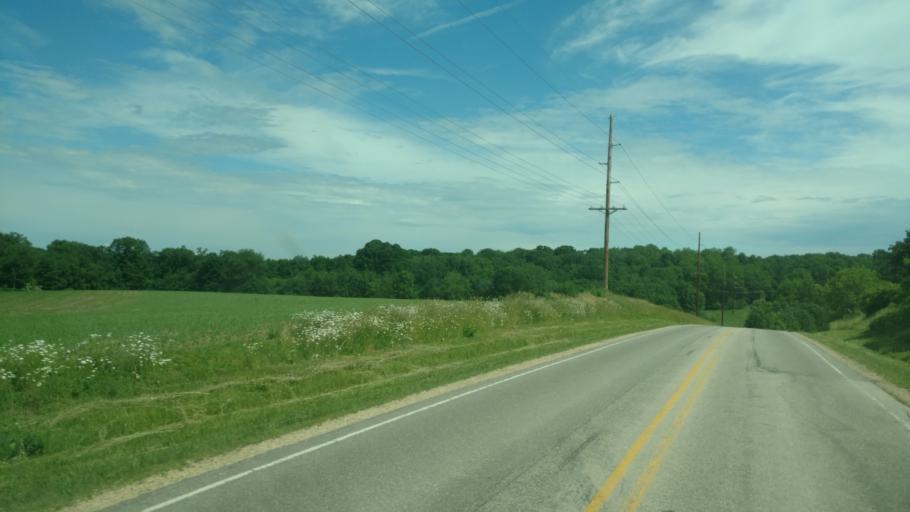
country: US
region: Wisconsin
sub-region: Vernon County
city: Hillsboro
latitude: 43.6706
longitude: -90.4583
